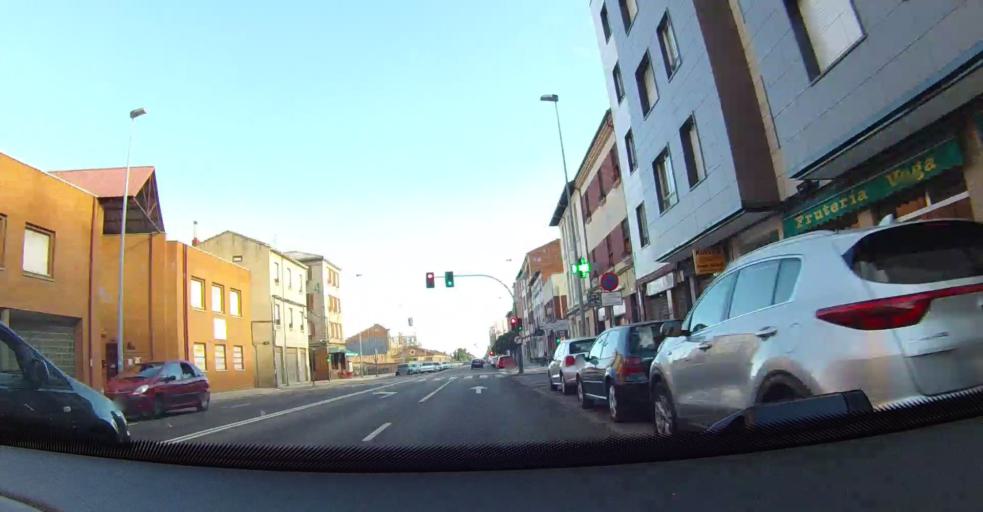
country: ES
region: Castille and Leon
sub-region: Provincia de Leon
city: Leon
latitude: 42.5963
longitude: -5.5854
